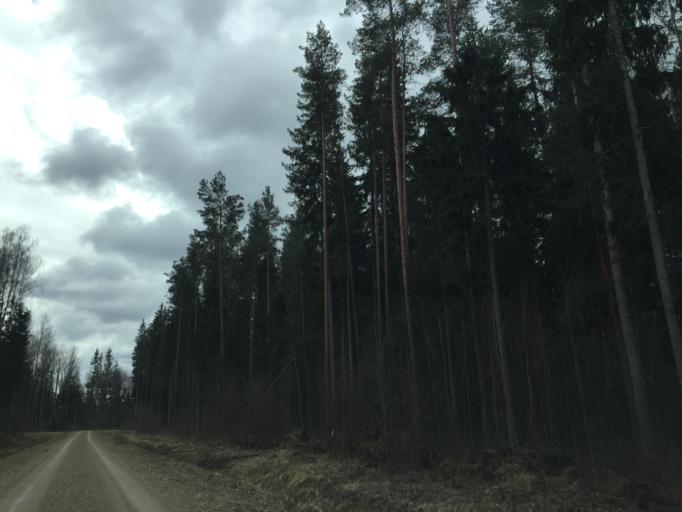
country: LV
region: Akniste
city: Akniste
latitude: 56.0781
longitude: 25.7618
